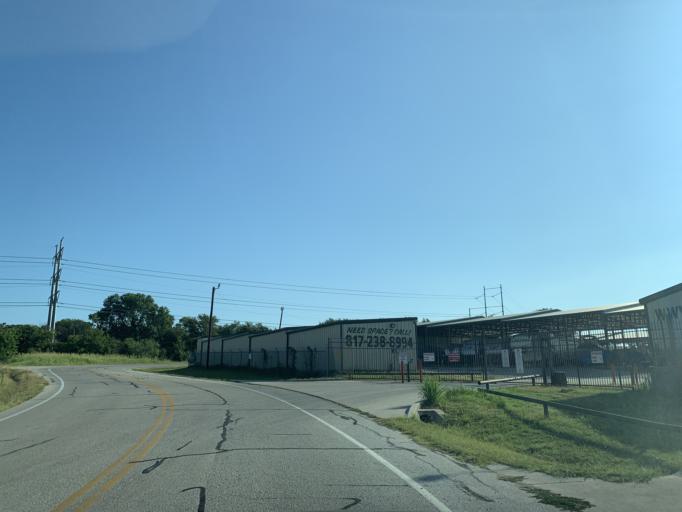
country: US
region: Texas
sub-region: Tarrant County
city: Lakeside
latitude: 32.8557
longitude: -97.5106
